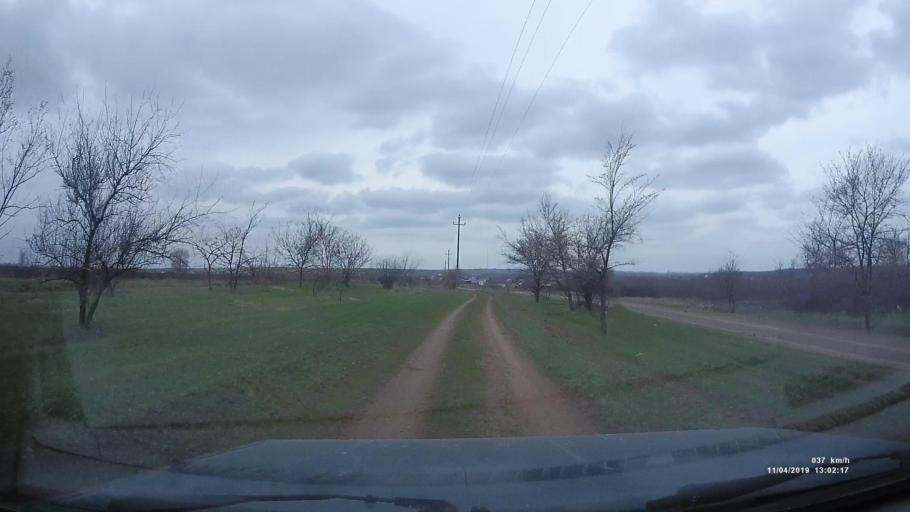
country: RU
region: Rostov
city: Staraya Stanitsa
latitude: 48.2877
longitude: 40.3594
